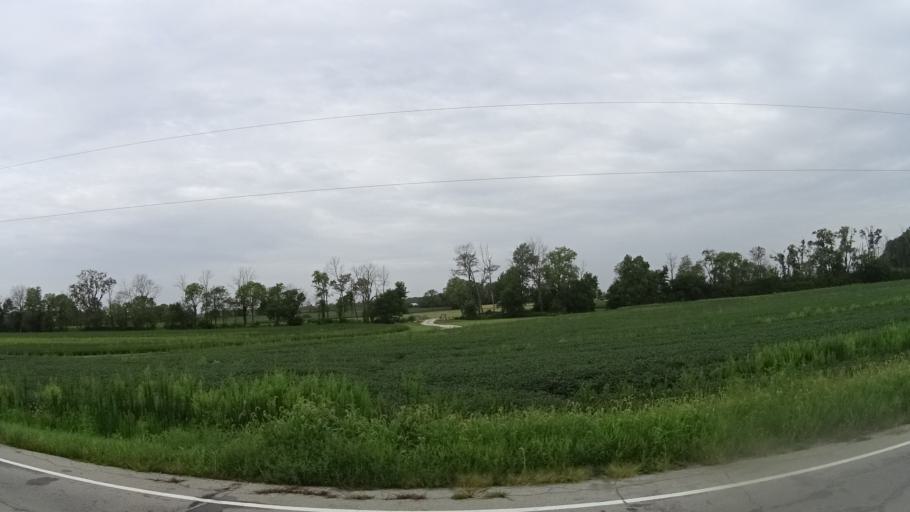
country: US
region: Indiana
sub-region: Madison County
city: Lapel
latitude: 40.0932
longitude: -85.8150
